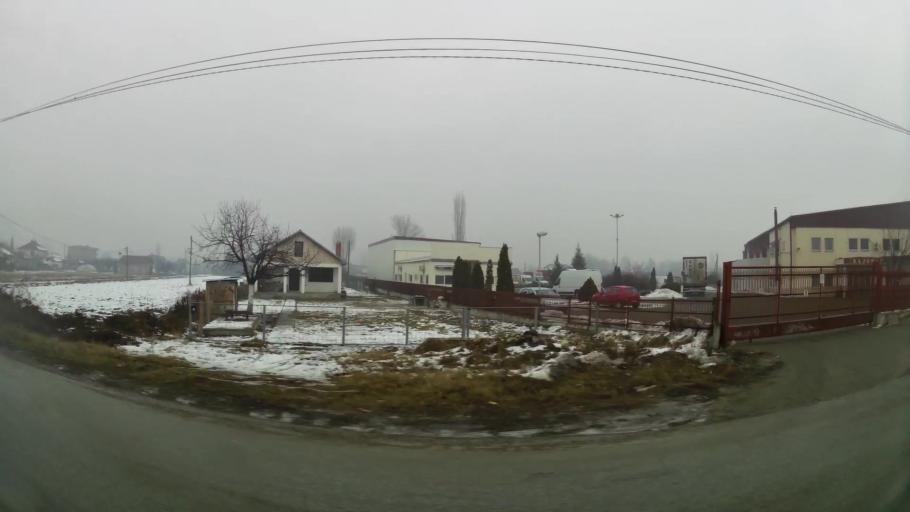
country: MK
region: Ilinden
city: Idrizovo
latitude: 41.9504
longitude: 21.5864
